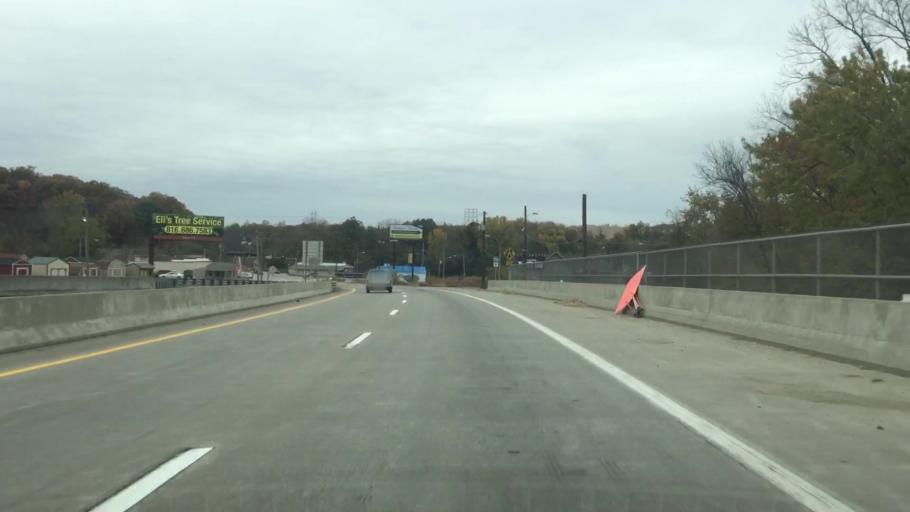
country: US
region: Missouri
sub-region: Jackson County
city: Raytown
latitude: 38.9640
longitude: -94.4265
